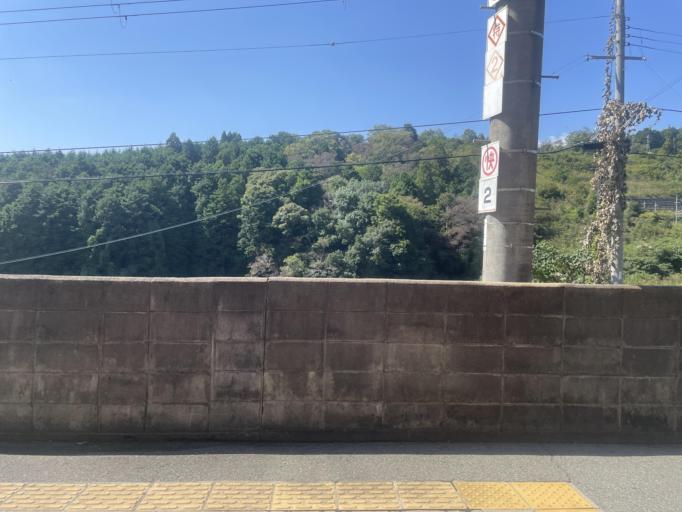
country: JP
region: Nara
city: Gose
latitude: 34.3880
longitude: 135.7665
